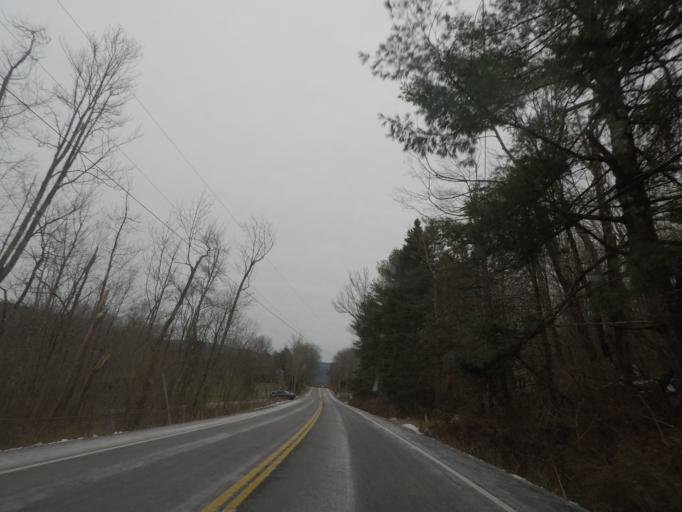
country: US
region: New York
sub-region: Rensselaer County
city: Hoosick Falls
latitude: 42.7564
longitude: -73.3624
